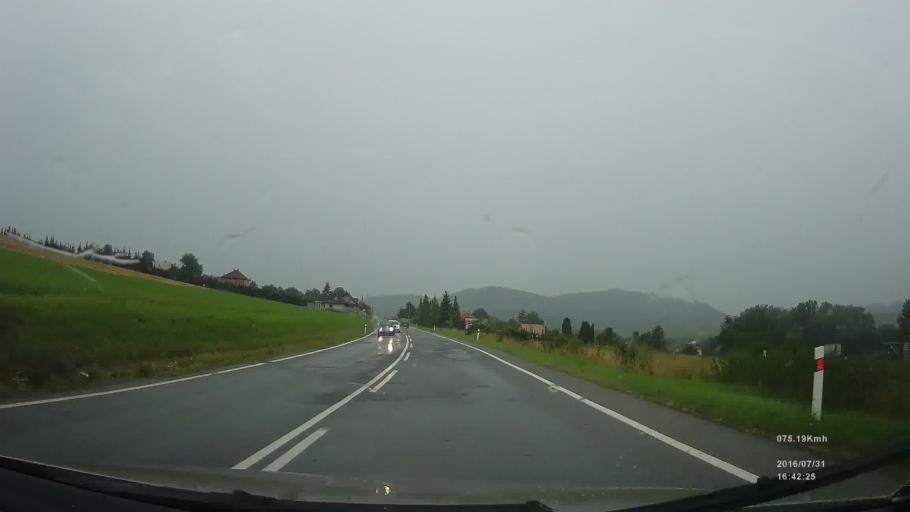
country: SK
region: Presovsky
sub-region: Okres Presov
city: Presov
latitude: 49.0940
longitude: 21.3117
